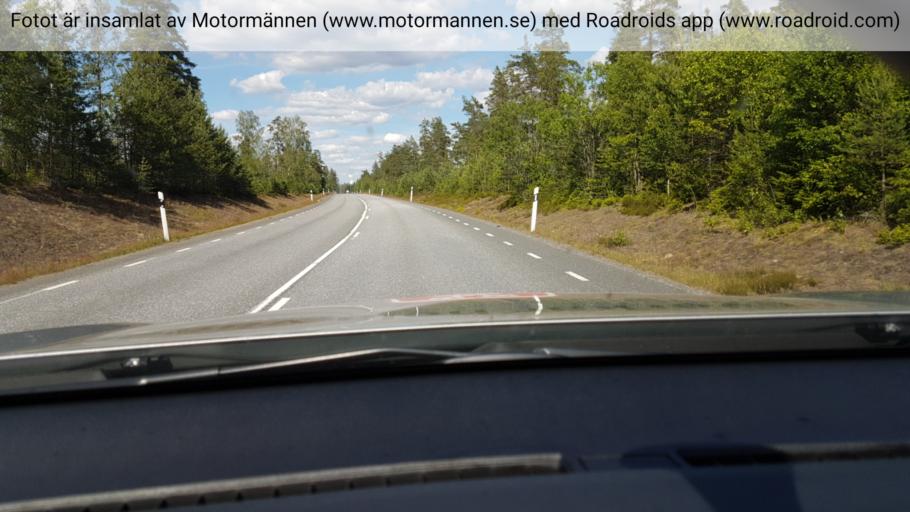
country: SE
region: Joenkoeping
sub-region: Vaggeryds Kommun
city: Skillingaryd
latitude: 57.4751
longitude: 14.1020
